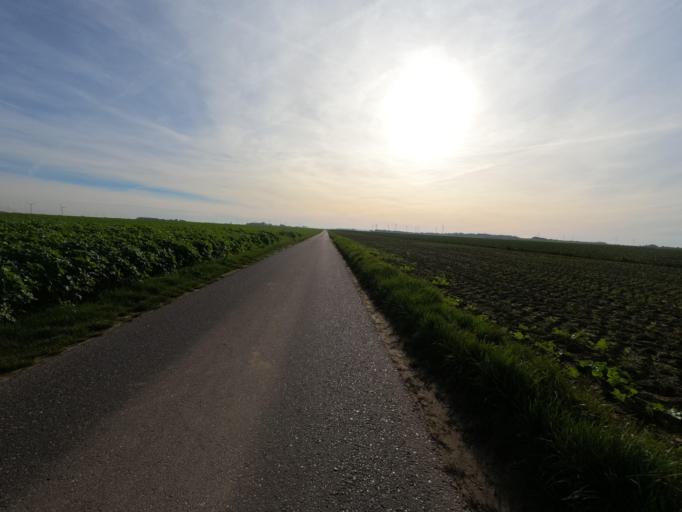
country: DE
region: North Rhine-Westphalia
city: Erkelenz
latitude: 51.0731
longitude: 6.3689
